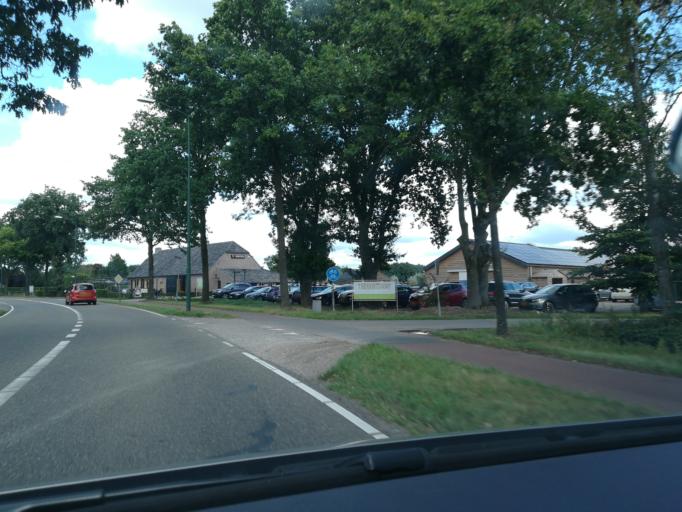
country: NL
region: North Brabant
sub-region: Gemeente Waalre
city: Waalre
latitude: 51.3744
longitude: 5.4470
